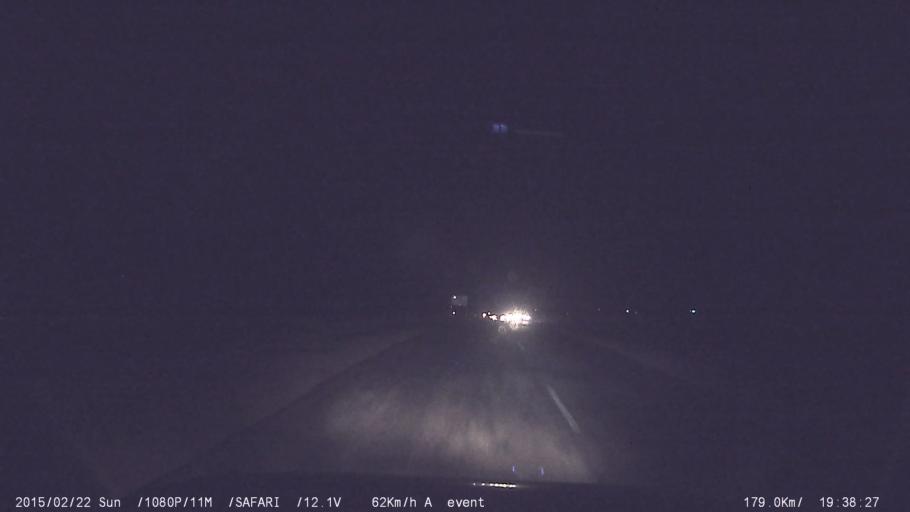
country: IN
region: Tamil Nadu
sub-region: Theni
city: Devadanappatti
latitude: 10.1432
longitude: 77.6310
